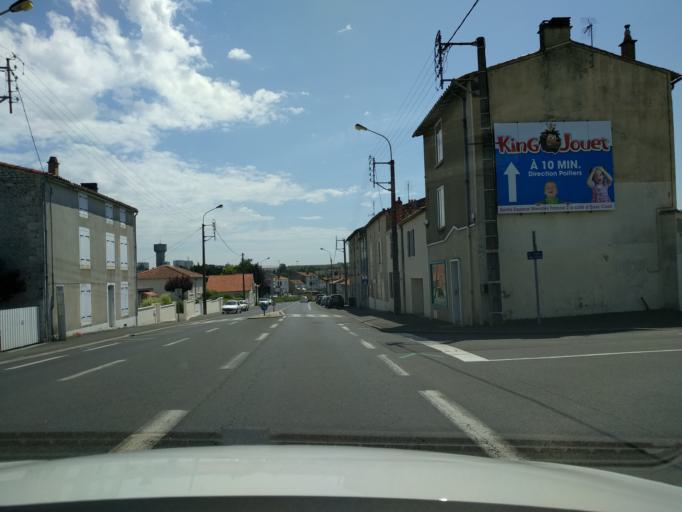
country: FR
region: Poitou-Charentes
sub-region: Departement des Deux-Sevres
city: Niort
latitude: 46.3359
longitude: -0.4748
